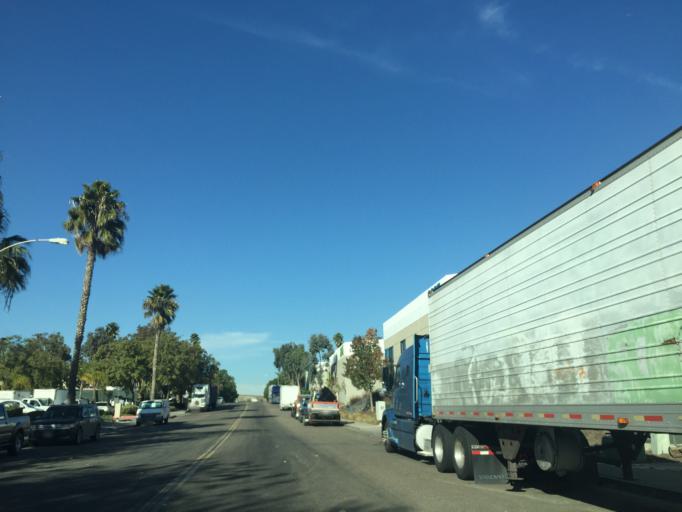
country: MX
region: Baja California
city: Tijuana
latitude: 32.5551
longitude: -116.9320
